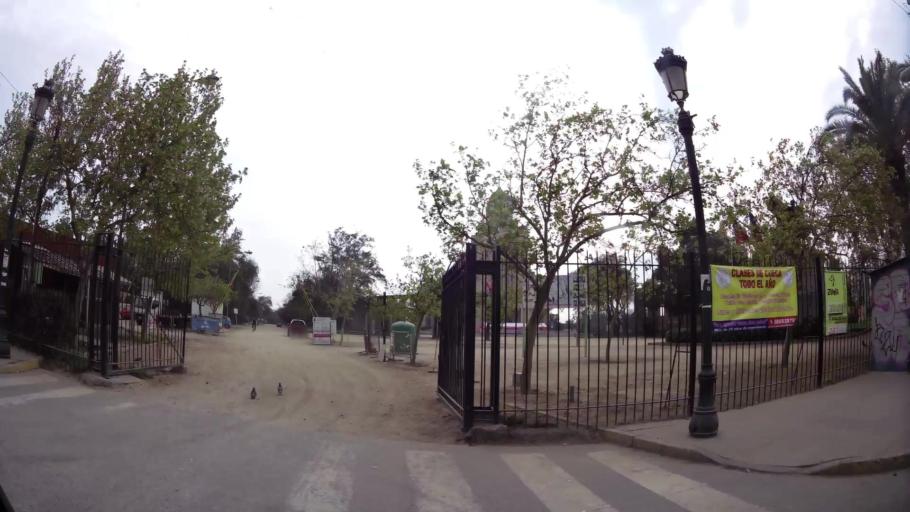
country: CL
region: Santiago Metropolitan
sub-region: Provincia de Santiago
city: Lo Prado
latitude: -33.5113
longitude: -70.7632
